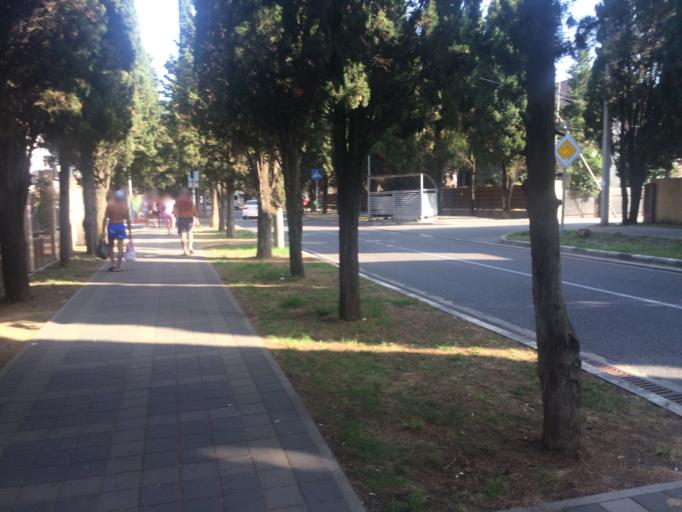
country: RU
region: Krasnodarskiy
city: Adler
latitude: 43.3919
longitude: 39.9825
